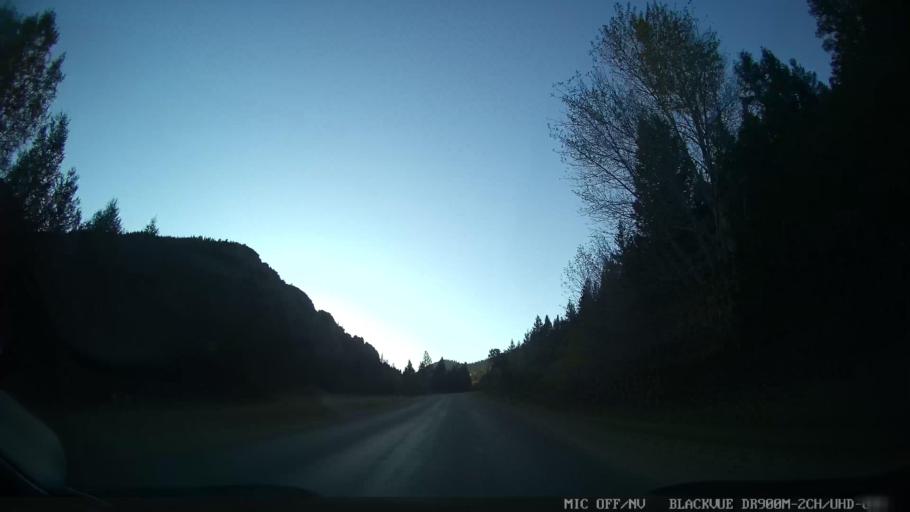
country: US
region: Colorado
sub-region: Grand County
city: Kremmling
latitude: 39.9981
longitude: -106.4808
